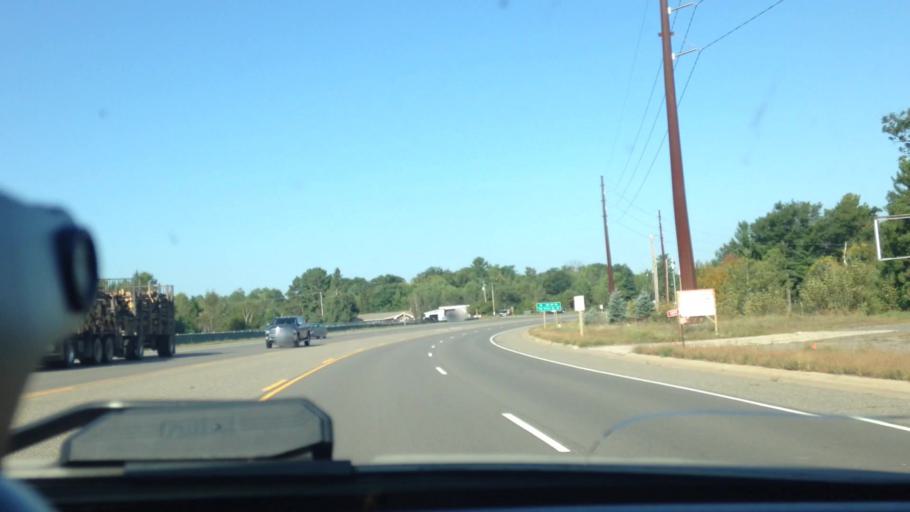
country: US
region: Michigan
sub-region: Dickinson County
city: Iron Mountain
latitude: 45.8820
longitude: -88.1394
